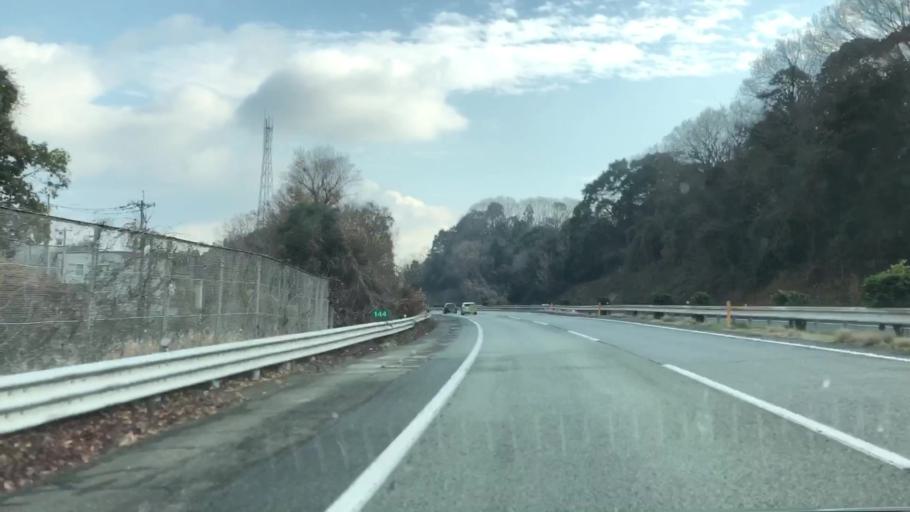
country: JP
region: Kumamoto
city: Tamana
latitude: 33.0037
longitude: 130.5844
